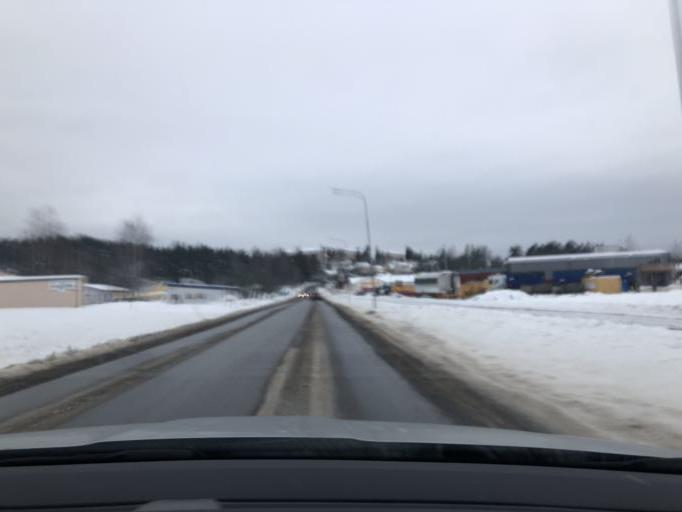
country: SE
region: OEstergoetland
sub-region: Kinda Kommun
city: Kisa
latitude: 57.9853
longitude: 15.6540
